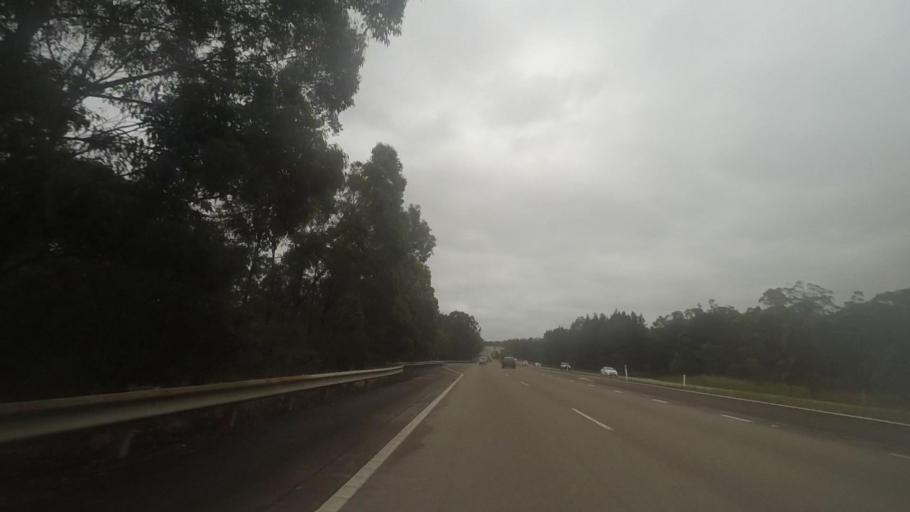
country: AU
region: New South Wales
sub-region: Port Stephens Shire
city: Medowie
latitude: -32.6790
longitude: 151.8202
